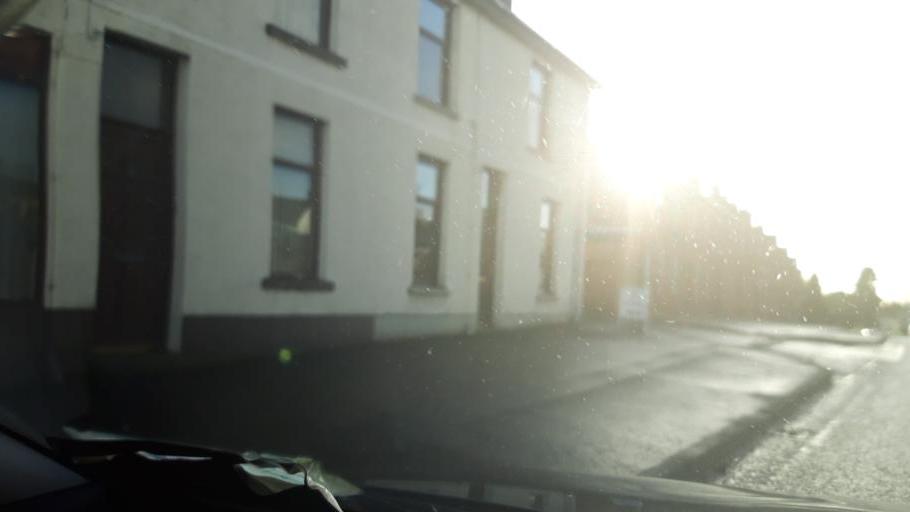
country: GB
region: Northern Ireland
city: Maghera
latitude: 54.8439
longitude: -6.6747
